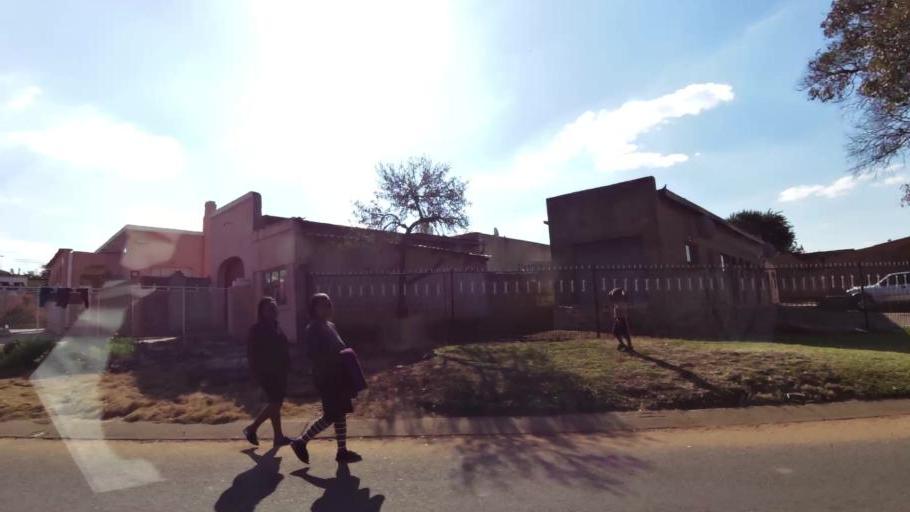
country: ZA
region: Gauteng
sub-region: City of Johannesburg Metropolitan Municipality
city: Soweto
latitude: -26.2372
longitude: 27.8738
